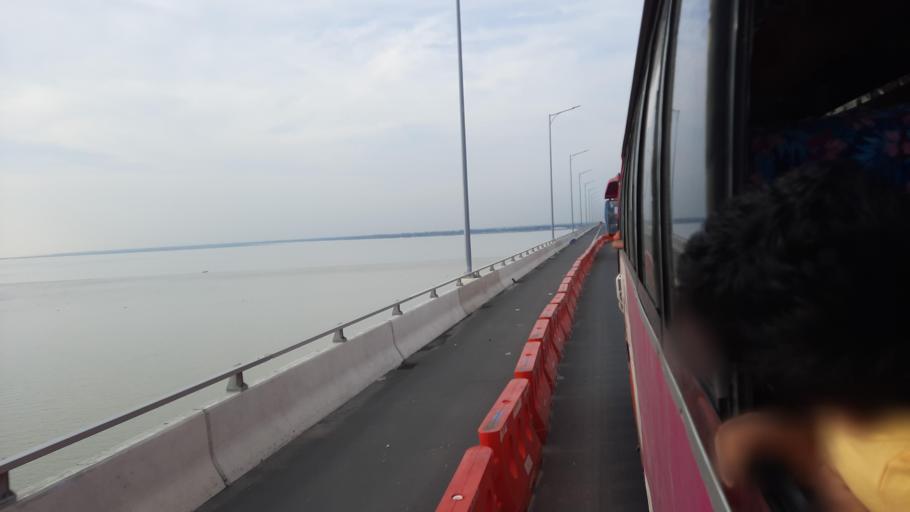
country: BD
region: Dhaka
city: Char Bhadrasan
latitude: 23.4427
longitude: 90.2615
